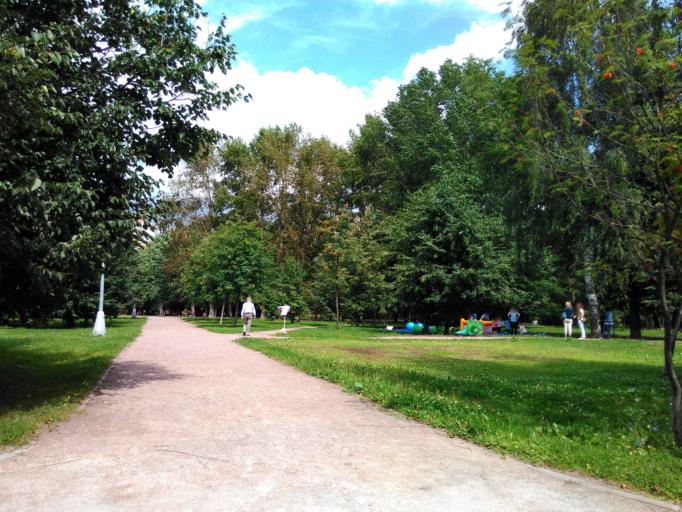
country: RU
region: Moskovskaya
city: Semenovskoye
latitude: 55.6657
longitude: 37.5334
